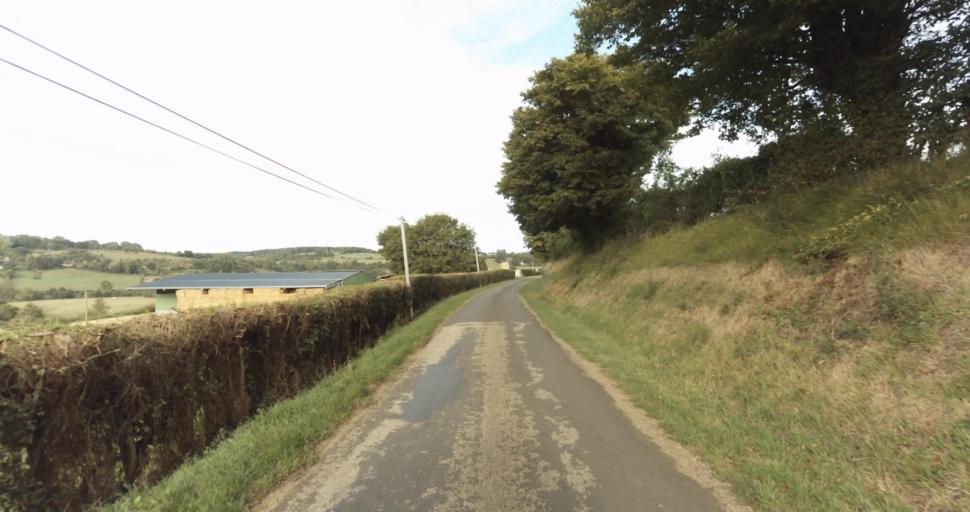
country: FR
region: Lower Normandy
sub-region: Departement de l'Orne
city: Vimoutiers
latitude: 48.8762
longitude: 0.2303
